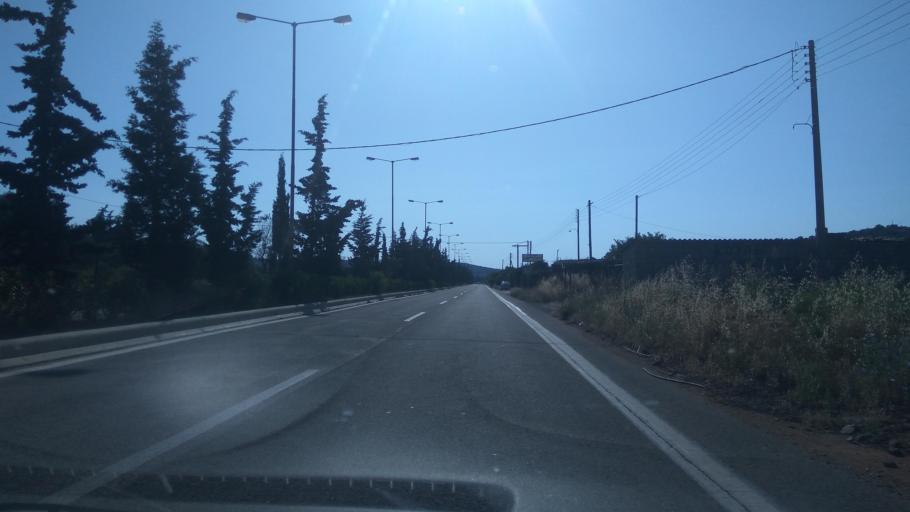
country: GR
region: Attica
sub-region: Nomarchia Anatolikis Attikis
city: Keratea
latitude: 37.8026
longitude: 24.0273
